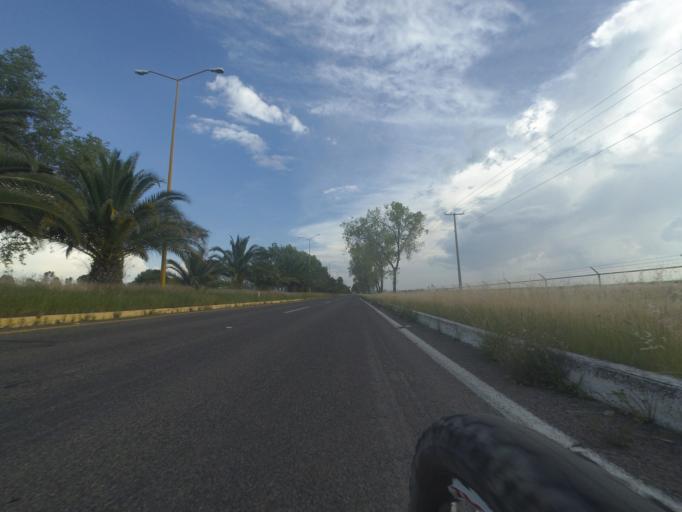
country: MX
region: Aguascalientes
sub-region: Aguascalientes
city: Penuelas (El Cienegal)
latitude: 21.7138
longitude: -102.3106
